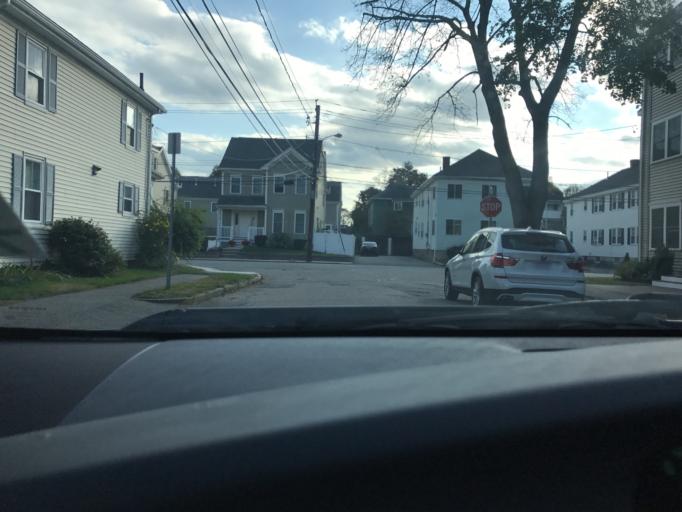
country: US
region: Massachusetts
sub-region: Middlesex County
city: Waltham
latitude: 42.3747
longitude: -71.2211
